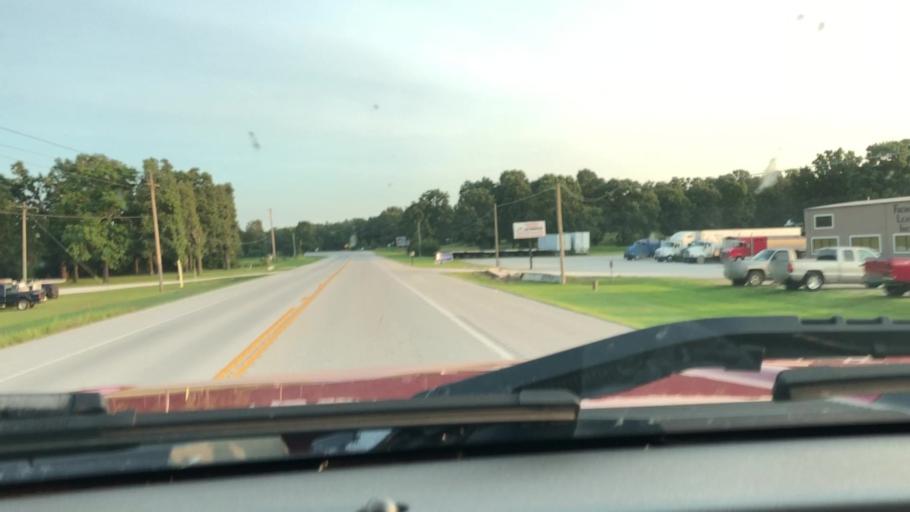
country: US
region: Missouri
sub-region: Jasper County
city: Duquesne
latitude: 36.9832
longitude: -94.4640
